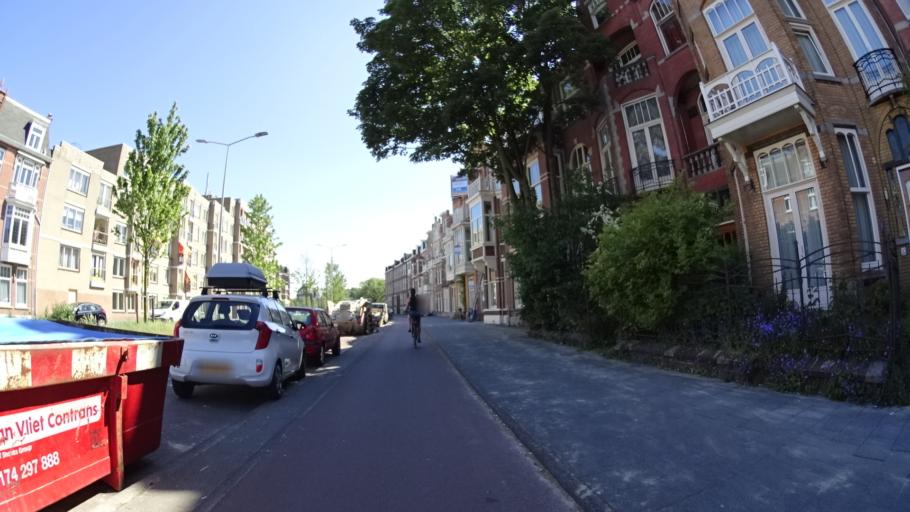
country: NL
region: South Holland
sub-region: Gemeente Den Haag
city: The Hague
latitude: 52.0812
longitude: 4.2763
